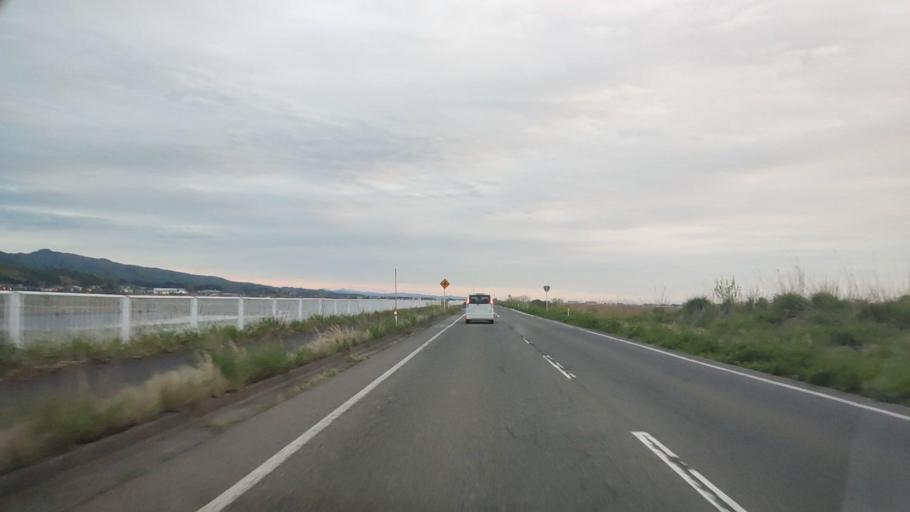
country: JP
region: Niigata
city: Niitsu-honcho
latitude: 37.7643
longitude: 139.0977
